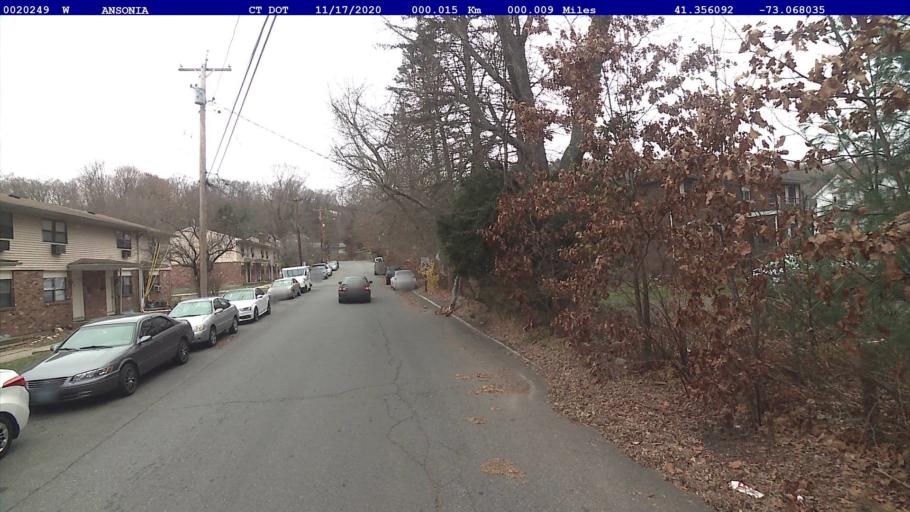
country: US
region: Connecticut
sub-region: New Haven County
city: Ansonia
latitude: 41.3561
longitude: -73.0680
